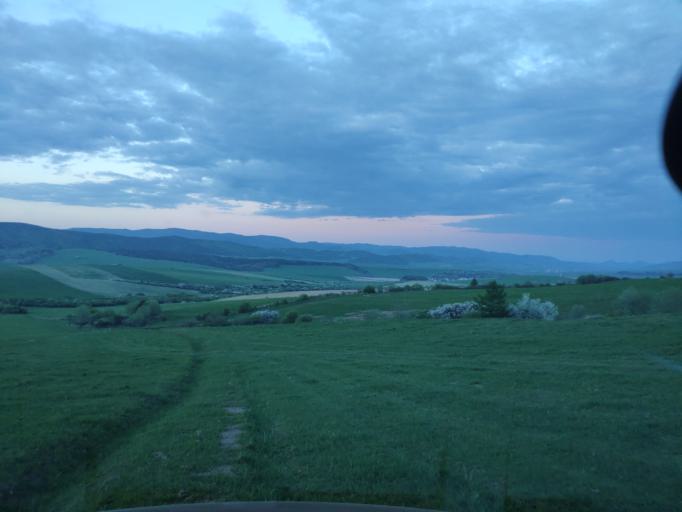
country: SK
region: Presovsky
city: Lipany
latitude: 49.1766
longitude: 20.8087
